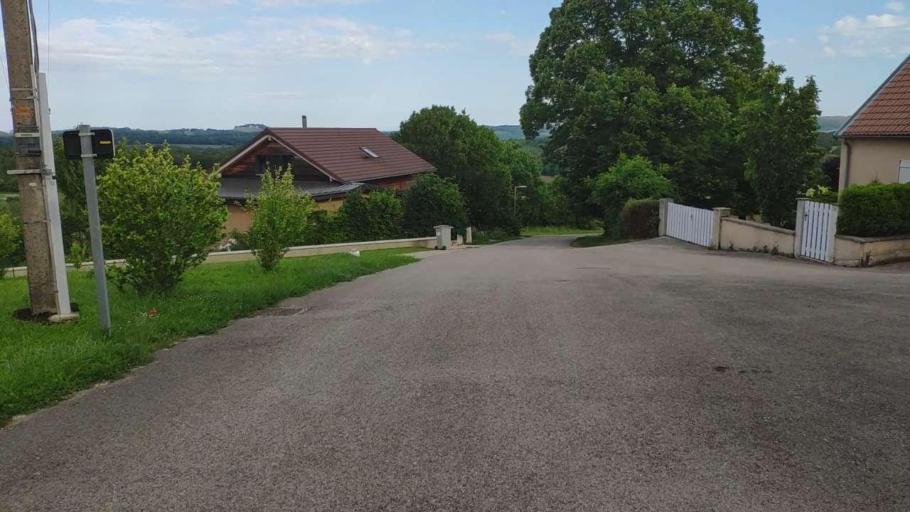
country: FR
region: Franche-Comte
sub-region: Departement du Jura
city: Perrigny
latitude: 46.7391
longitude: 5.6021
